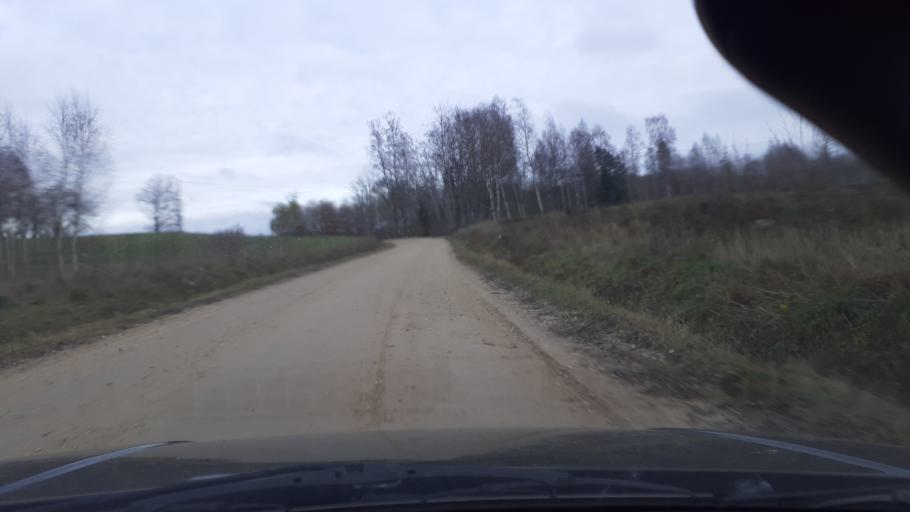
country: LV
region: Alsunga
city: Alsunga
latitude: 56.9518
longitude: 21.6459
